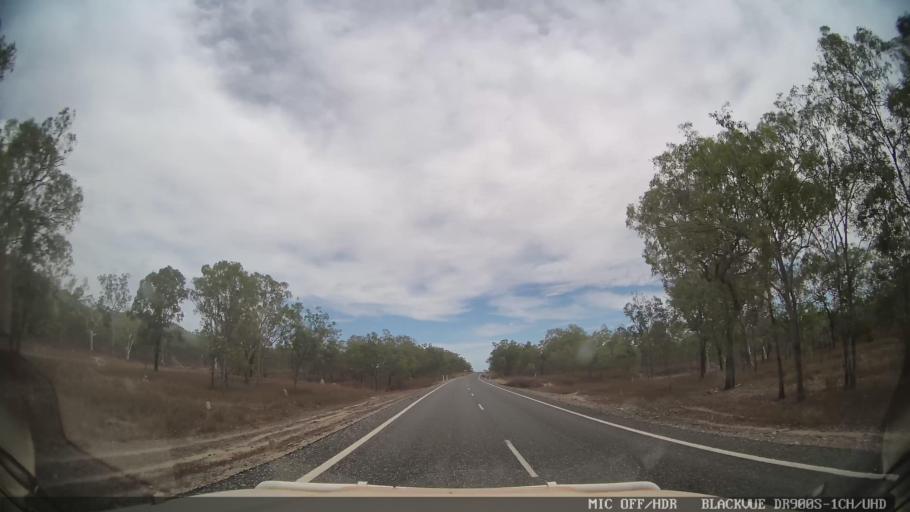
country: AU
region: Queensland
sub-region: Cairns
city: Port Douglas
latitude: -16.2535
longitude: 144.7253
